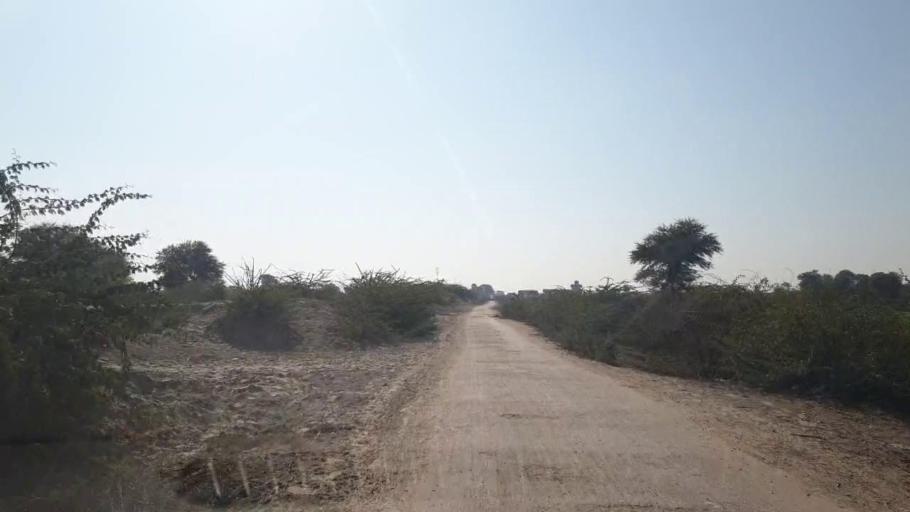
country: PK
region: Sindh
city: Shahpur Chakar
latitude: 26.0813
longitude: 68.6477
